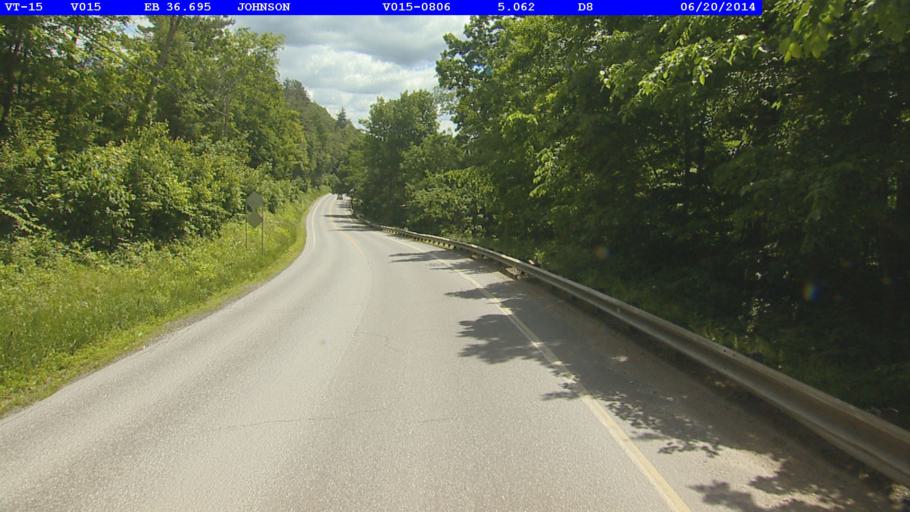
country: US
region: Vermont
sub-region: Lamoille County
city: Johnson
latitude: 44.6237
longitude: -72.6754
